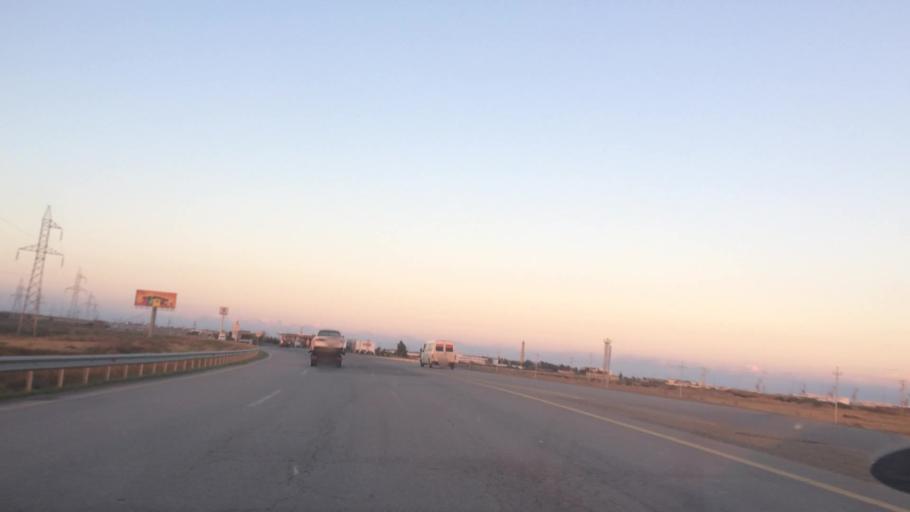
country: AZ
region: Baki
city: Qobustan
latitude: 39.9672
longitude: 49.4122
